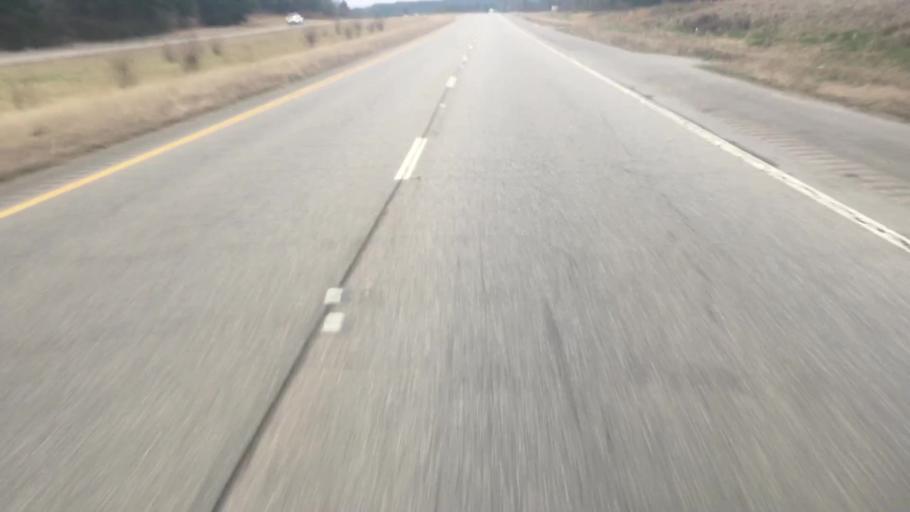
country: US
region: Alabama
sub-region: Walker County
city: Dora
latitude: 33.7988
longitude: -87.1137
